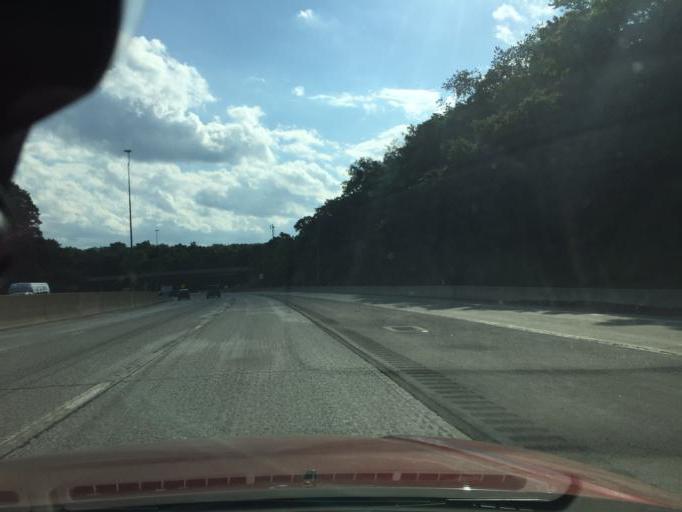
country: US
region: New York
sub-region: Westchester County
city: Mamaroneck
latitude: 40.9621
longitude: -73.7368
